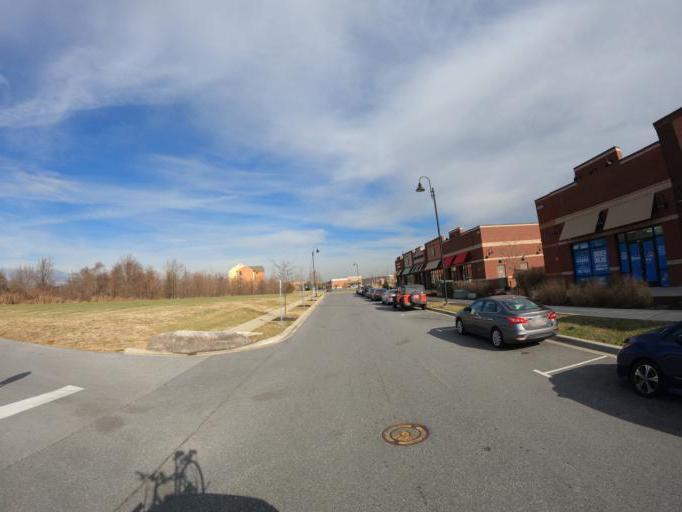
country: US
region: Maryland
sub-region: Frederick County
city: Ballenger Creek
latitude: 39.3693
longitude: -77.4146
